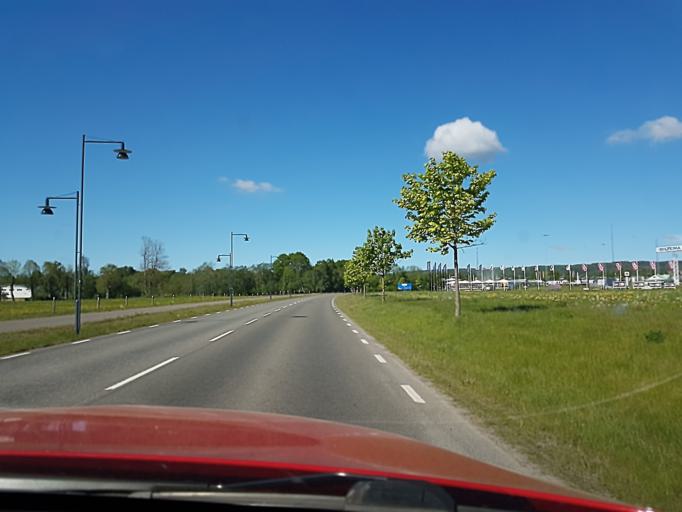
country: SE
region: Vaestra Goetaland
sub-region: Skovde Kommun
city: Skoevde
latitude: 58.4079
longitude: 13.8831
